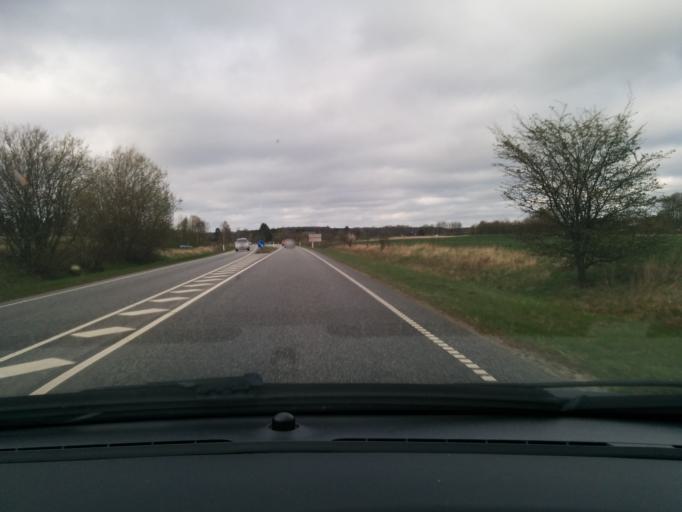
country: DK
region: Central Jutland
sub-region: Favrskov Kommune
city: Hammel
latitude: 56.2394
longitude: 9.8705
